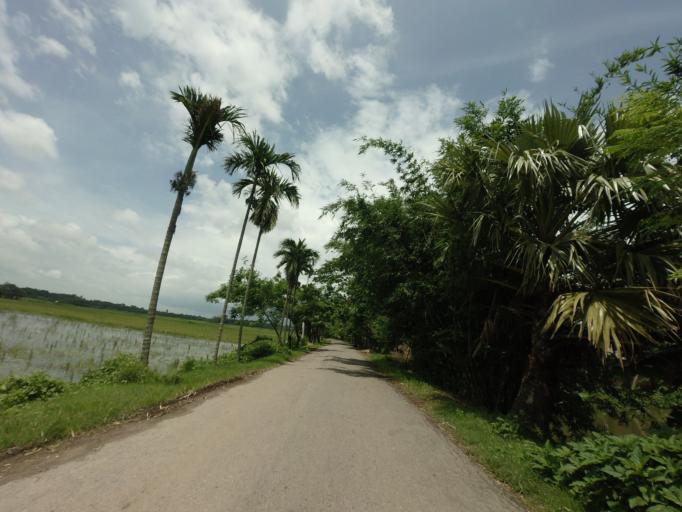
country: BD
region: Khulna
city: Kalia
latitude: 23.0410
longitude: 89.6462
